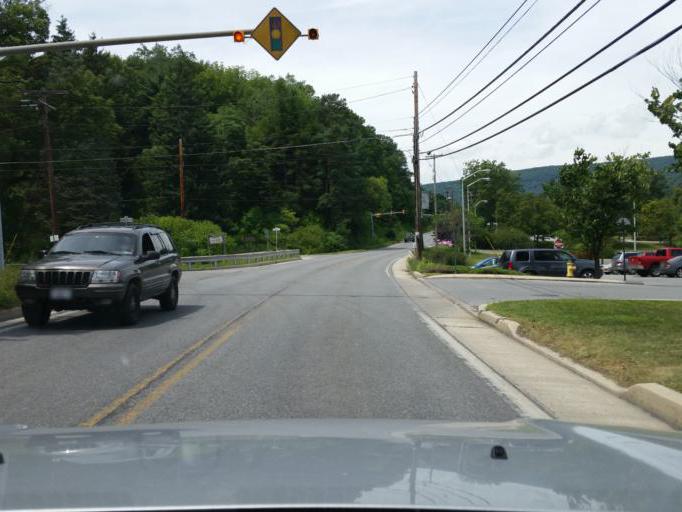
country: US
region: Pennsylvania
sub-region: Blair County
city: Altoona
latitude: 40.5381
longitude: -78.4085
